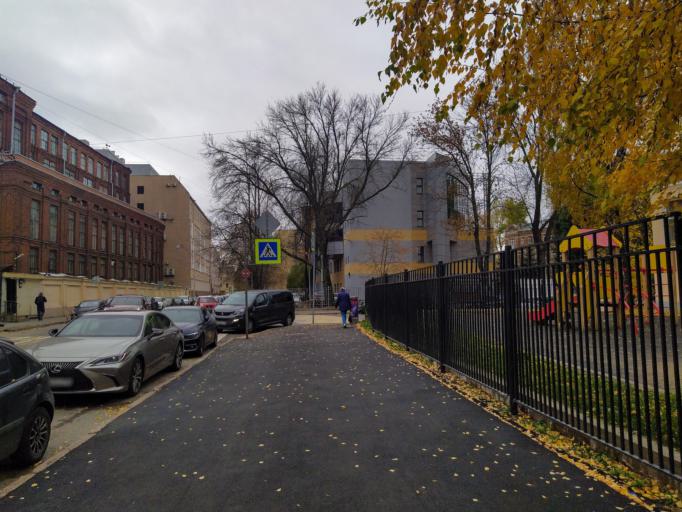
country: RU
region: St.-Petersburg
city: Petrogradka
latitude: 59.9631
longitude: 30.3300
